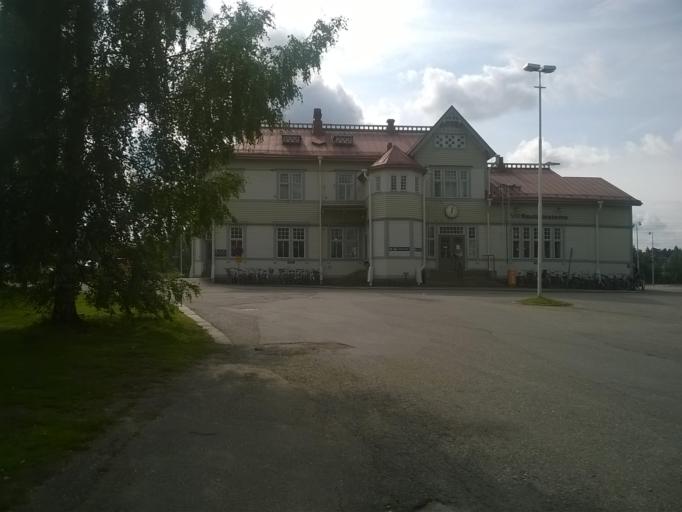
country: FI
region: Kainuu
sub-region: Kajaani
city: Kajaani
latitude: 64.2204
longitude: 27.7385
